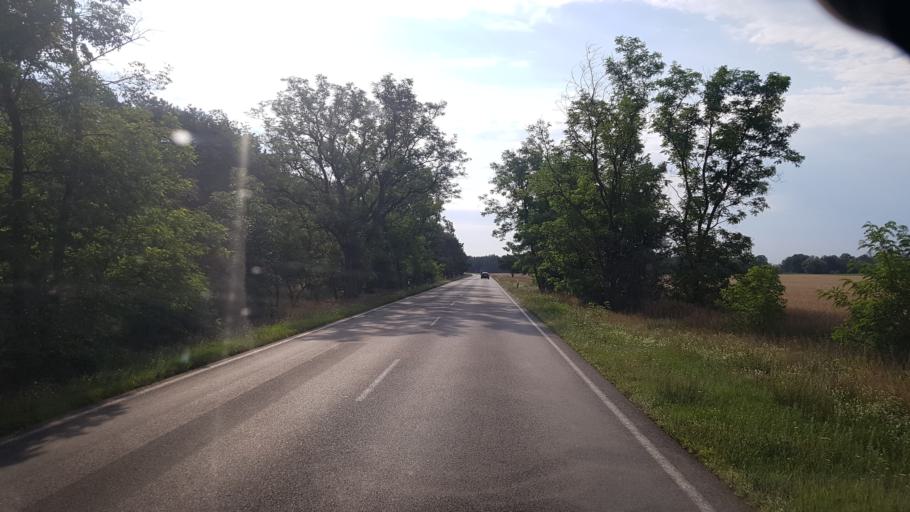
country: DE
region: Brandenburg
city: Baruth
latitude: 52.0545
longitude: 13.5726
